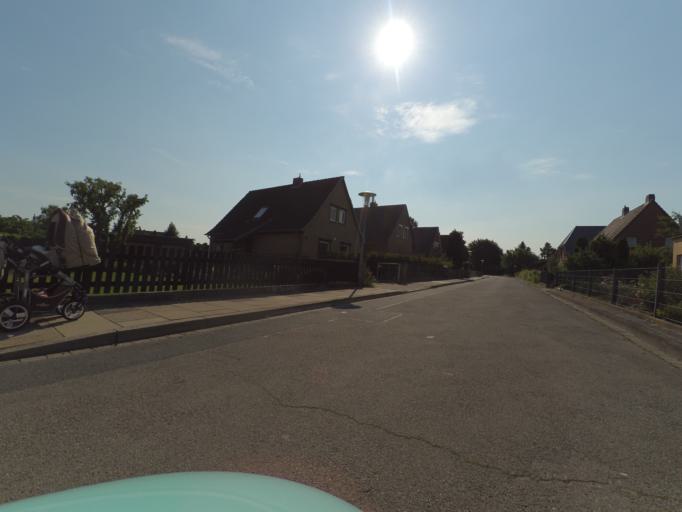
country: DE
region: Lower Saxony
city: Burgdorf
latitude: 52.4394
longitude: 10.0097
